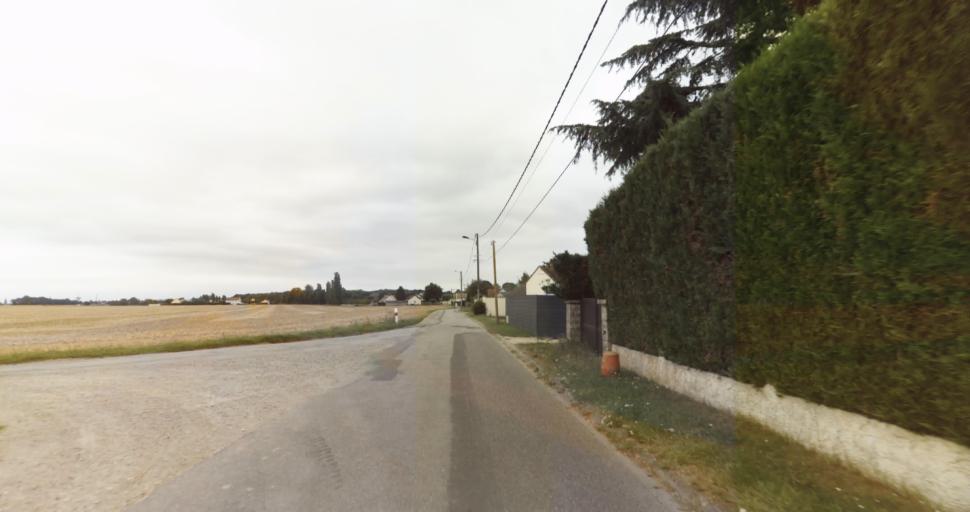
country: FR
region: Haute-Normandie
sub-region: Departement de l'Eure
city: La Couture-Boussey
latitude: 48.9129
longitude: 1.3908
